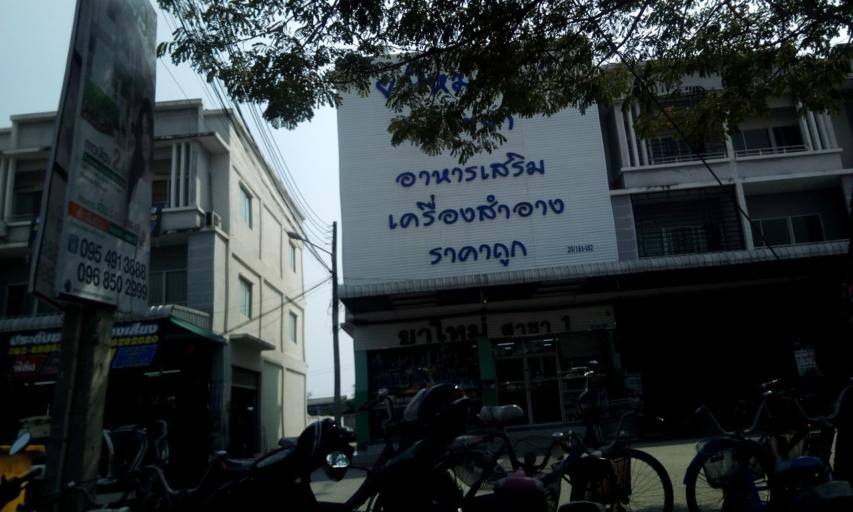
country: TH
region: Pathum Thani
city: Lam Luk Ka
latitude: 13.9647
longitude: 100.7388
